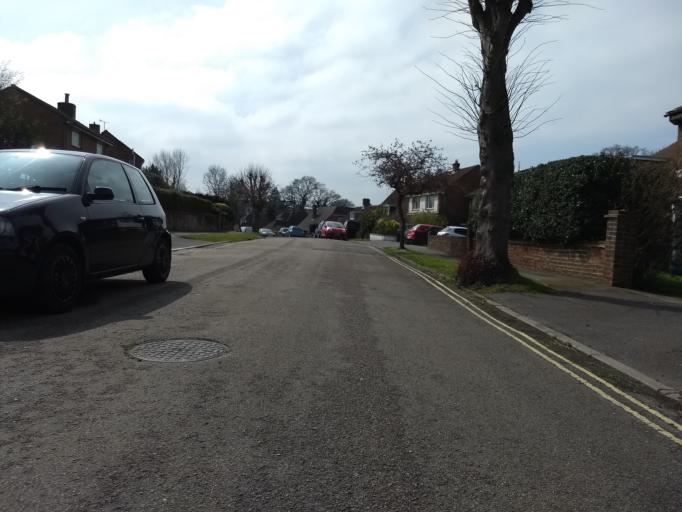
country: GB
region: England
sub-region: Isle of Wight
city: Ryde
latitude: 50.7288
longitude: -1.1710
